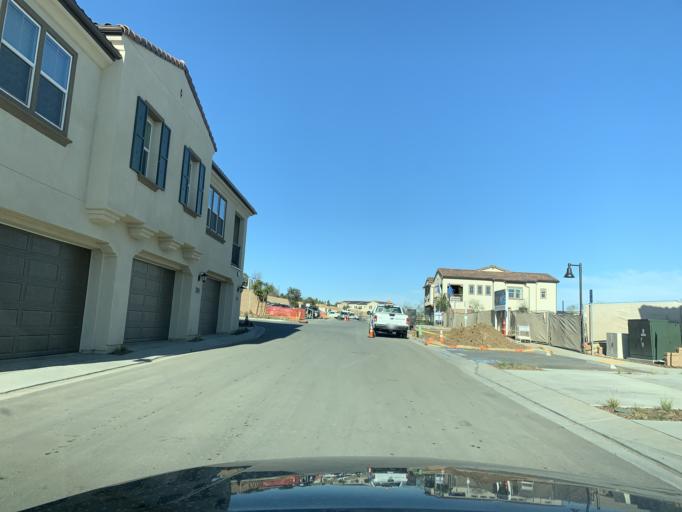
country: US
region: California
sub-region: San Diego County
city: Poway
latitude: 32.9712
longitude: -117.0933
